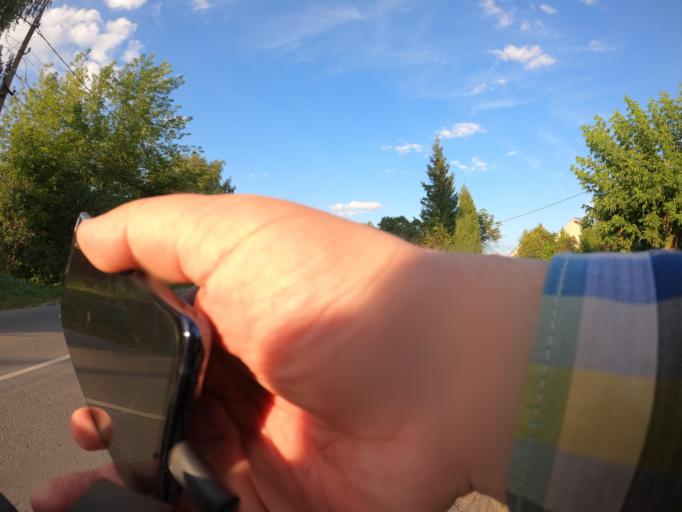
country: RU
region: Moskovskaya
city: Raduzhnyy
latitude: 55.1017
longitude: 38.7313
